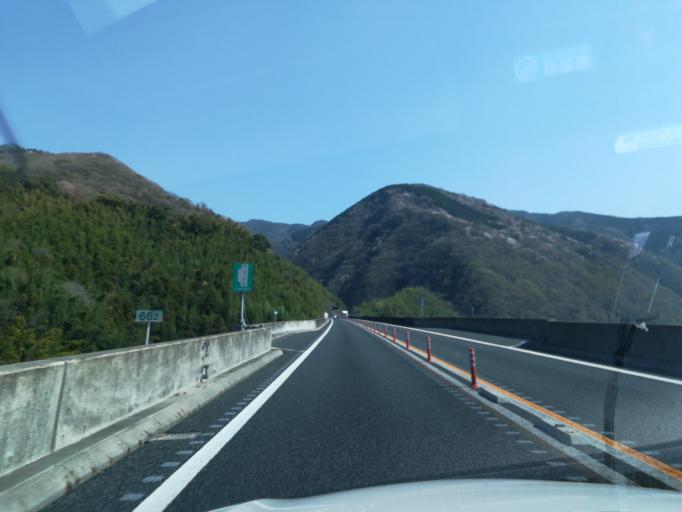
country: JP
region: Tokushima
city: Ikedacho
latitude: 34.0466
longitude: 133.9132
